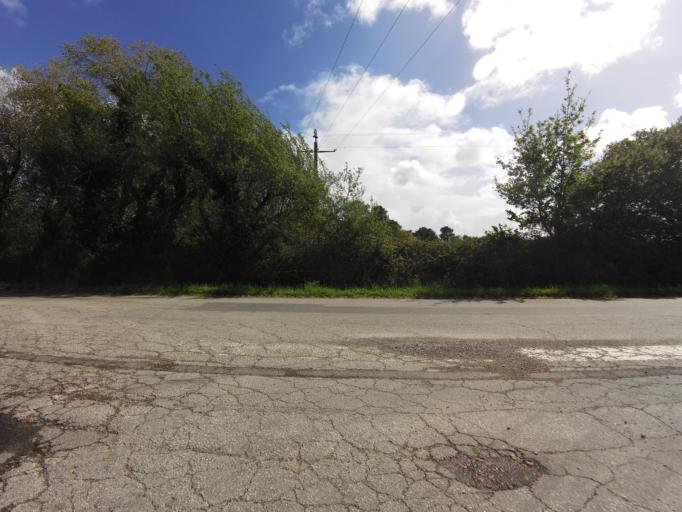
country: FR
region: Brittany
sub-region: Departement du Morbihan
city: Plougoumelen
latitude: 47.6523
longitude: -2.9014
